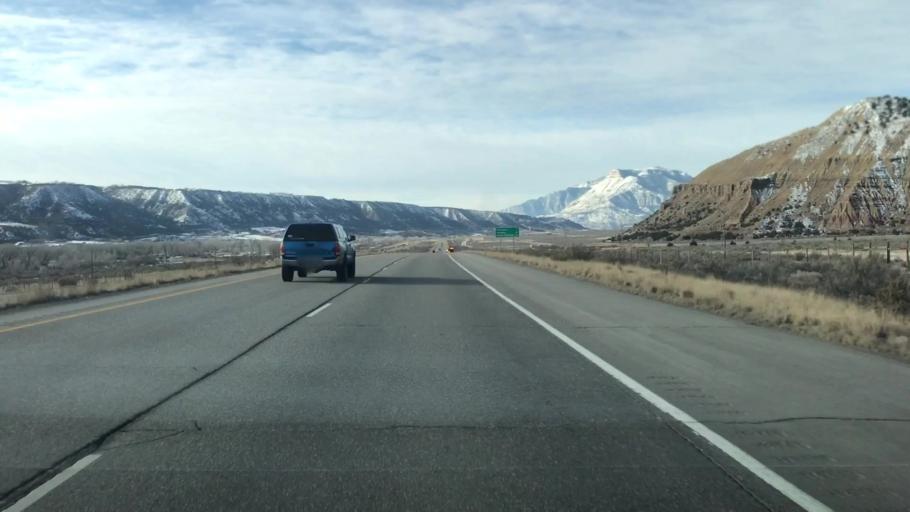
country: US
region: Colorado
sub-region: Garfield County
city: Battlement Mesa
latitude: 39.4908
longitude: -107.9527
